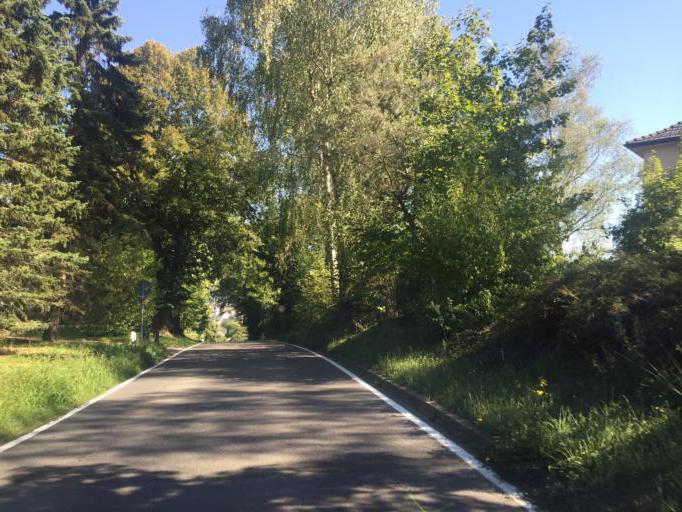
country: CH
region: Thurgau
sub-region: Frauenfeld District
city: Diessenhofen
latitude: 47.6952
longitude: 8.7370
